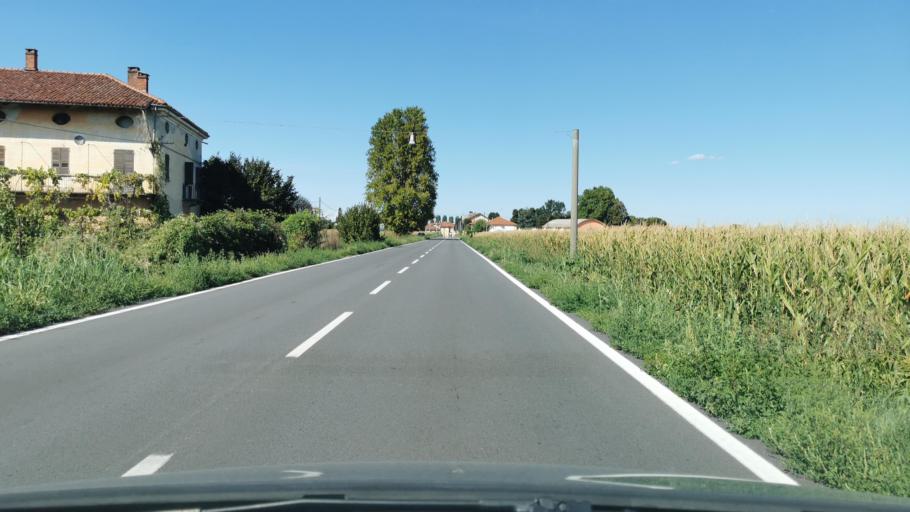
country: IT
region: Piedmont
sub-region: Provincia di Cuneo
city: Vottignasco
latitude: 44.5512
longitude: 7.6191
